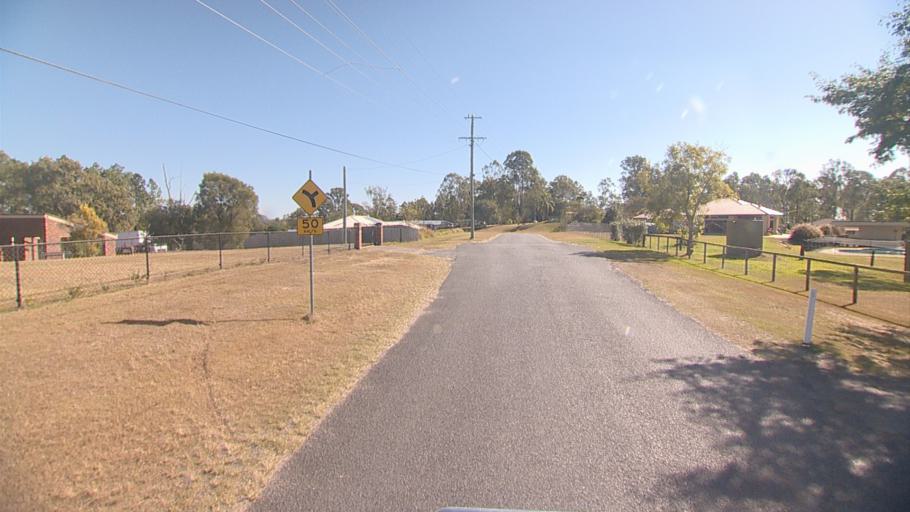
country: AU
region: Queensland
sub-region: Logan
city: Cedar Vale
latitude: -27.8548
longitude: 153.0141
